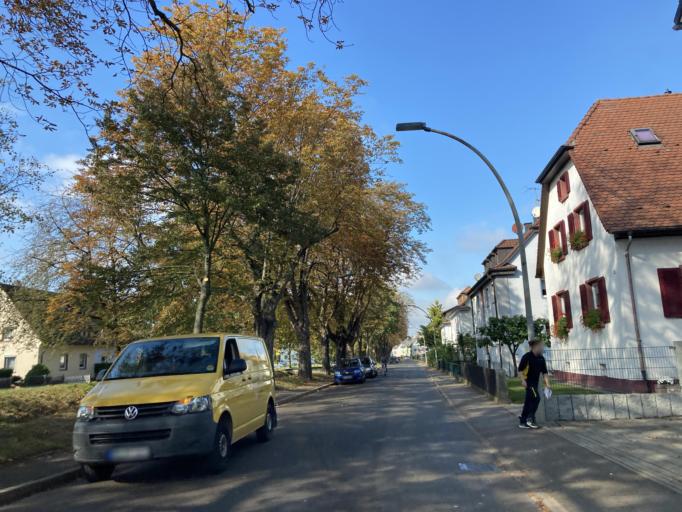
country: DE
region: Baden-Wuerttemberg
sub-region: Freiburg Region
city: Heitersheim
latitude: 47.8763
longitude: 7.6534
